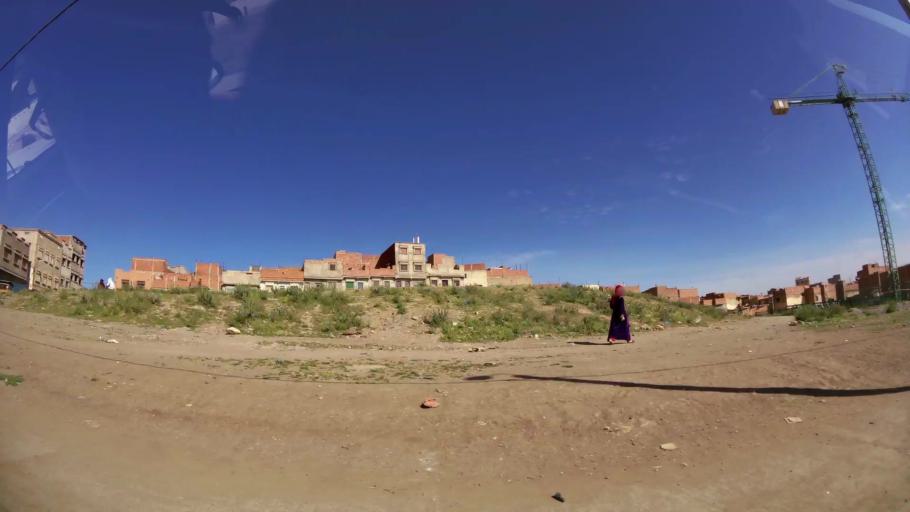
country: MA
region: Oriental
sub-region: Oujda-Angad
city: Oujda
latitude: 34.6493
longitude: -1.9425
